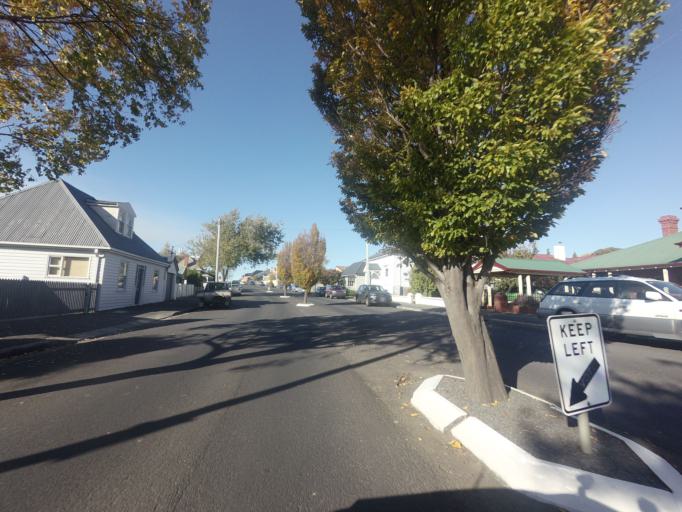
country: AU
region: Tasmania
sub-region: Hobart
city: Sandy Bay
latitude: -42.8841
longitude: 147.3132
